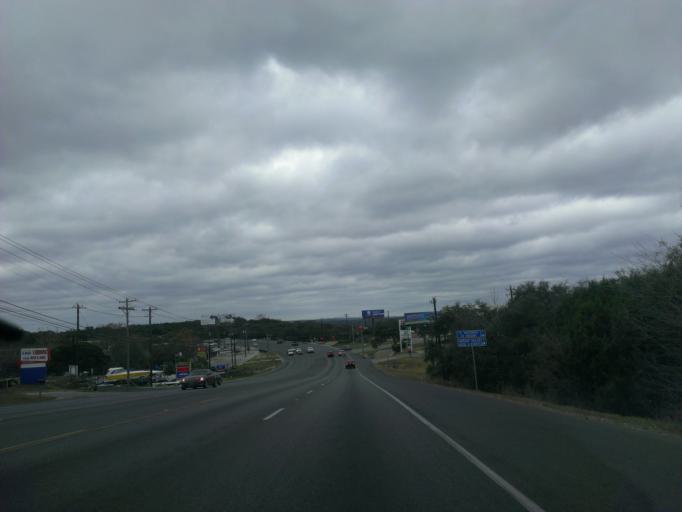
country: US
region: Texas
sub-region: Travis County
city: Hudson Bend
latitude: 30.3973
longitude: -97.9263
